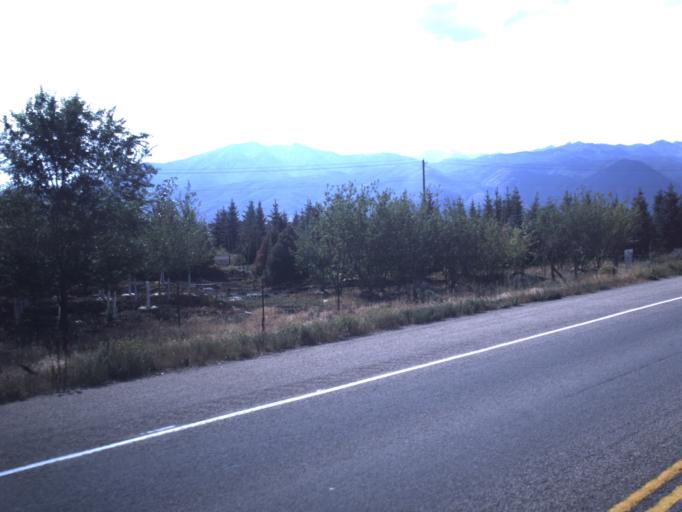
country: US
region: Utah
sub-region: Wasatch County
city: Heber
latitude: 40.4738
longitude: -111.3938
